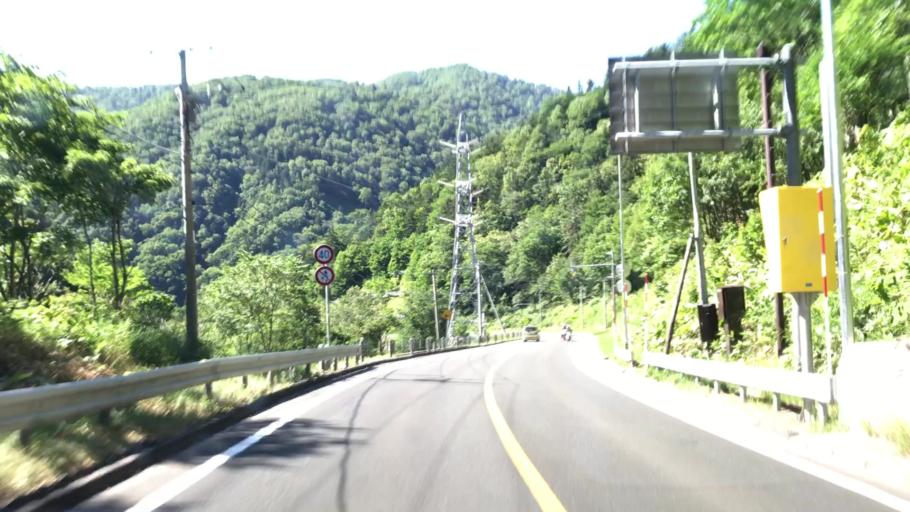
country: JP
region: Hokkaido
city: Shimo-furano
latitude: 42.9647
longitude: 142.6383
